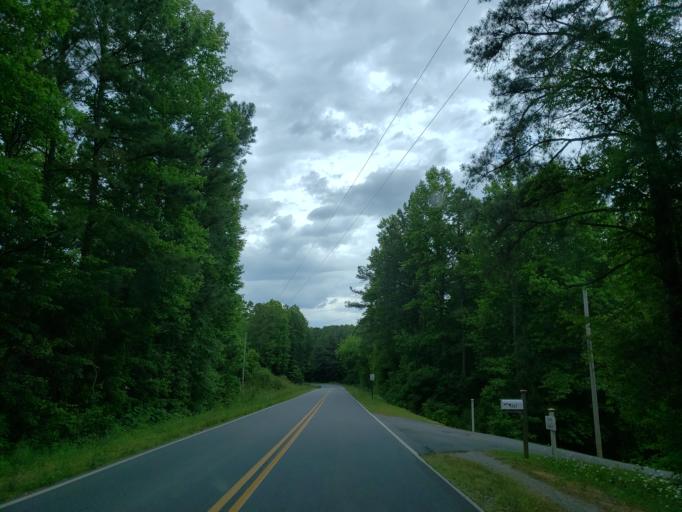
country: US
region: Georgia
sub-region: Polk County
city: Rockmart
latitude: 33.9529
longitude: -85.0420
